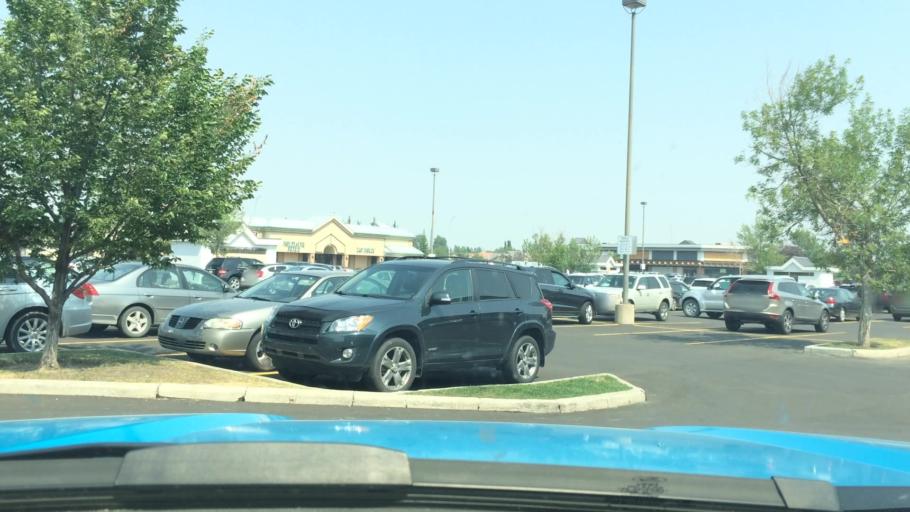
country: CA
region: Alberta
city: Calgary
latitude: 51.1375
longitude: -114.1594
